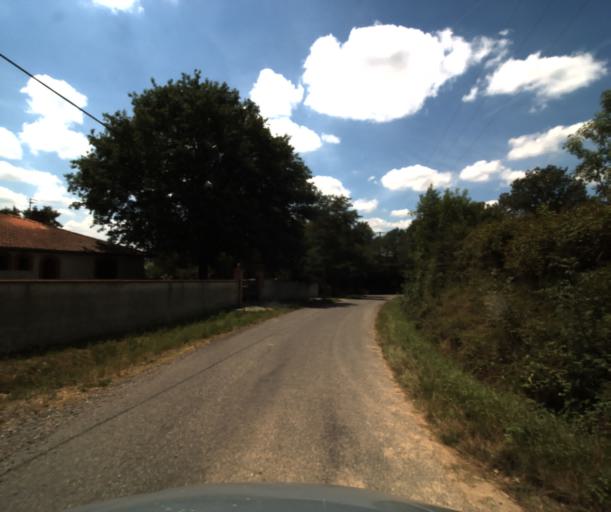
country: FR
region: Midi-Pyrenees
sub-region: Departement de la Haute-Garonne
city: Saint-Lys
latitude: 43.4860
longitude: 1.1831
